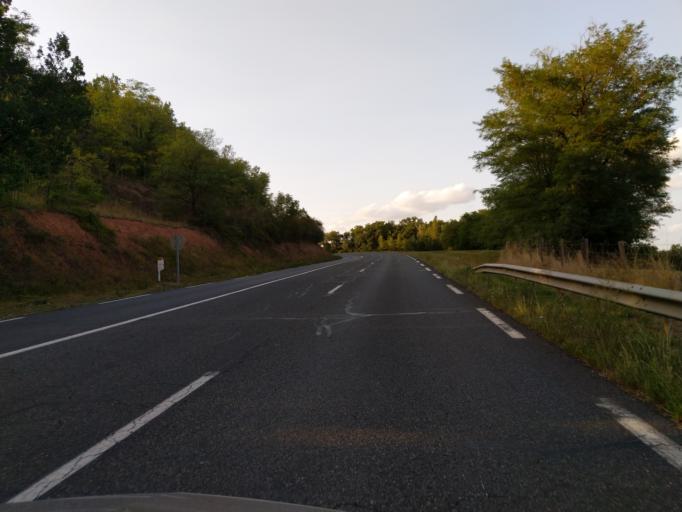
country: FR
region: Midi-Pyrenees
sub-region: Departement du Tarn
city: Realmont
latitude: 43.7984
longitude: 2.1866
